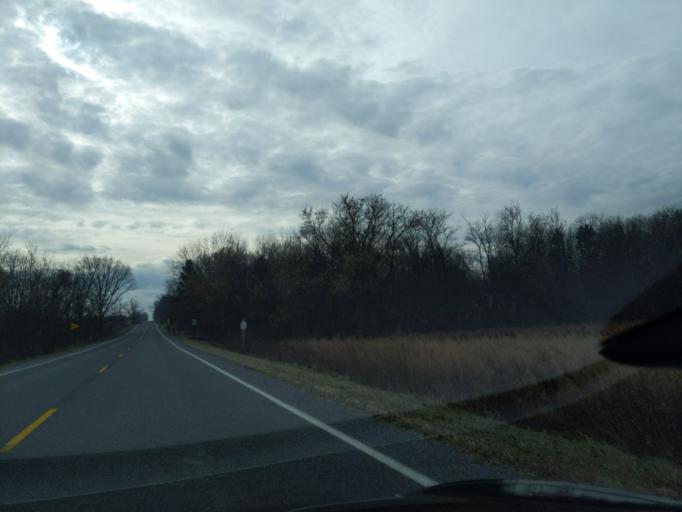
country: US
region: Michigan
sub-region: Ingham County
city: Holt
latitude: 42.5635
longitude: -84.5228
